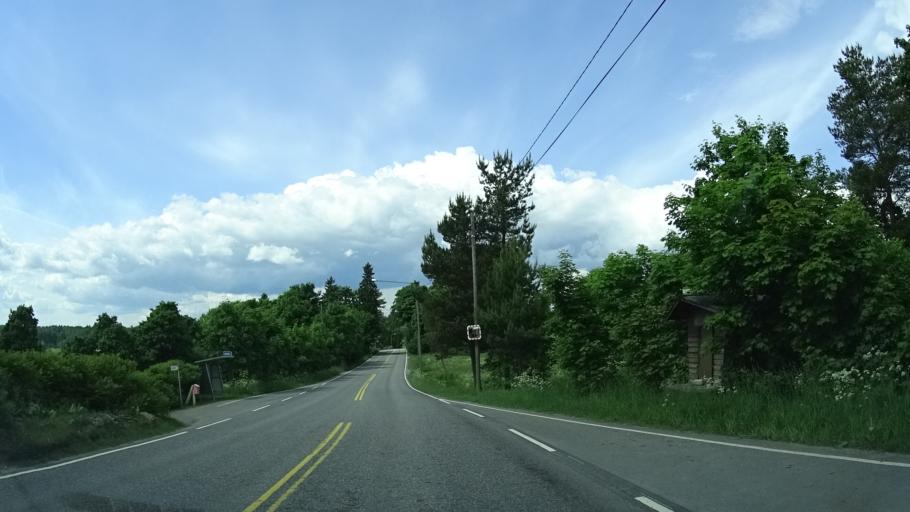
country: FI
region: Uusimaa
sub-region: Helsinki
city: Kirkkonummi
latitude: 60.2208
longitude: 24.4716
